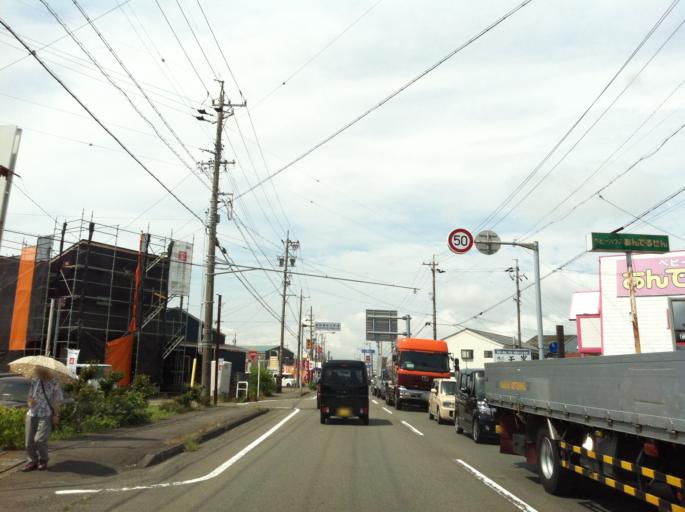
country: JP
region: Shizuoka
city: Yaizu
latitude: 34.8292
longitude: 138.3000
